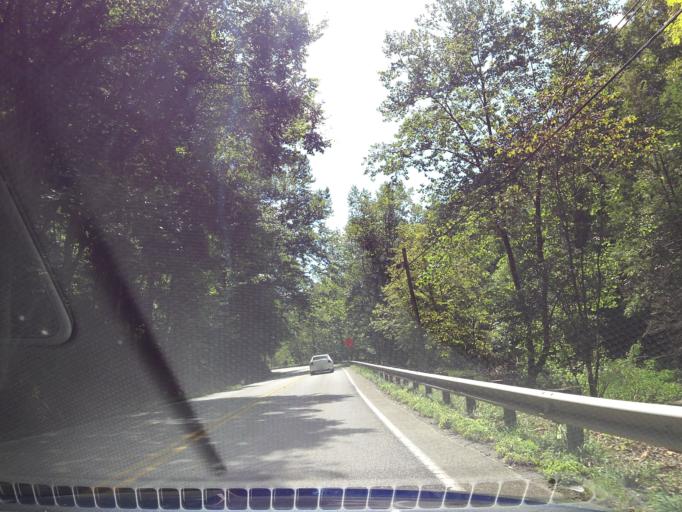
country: US
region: Kentucky
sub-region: Harlan County
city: Loyall
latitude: 36.9669
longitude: -83.3950
